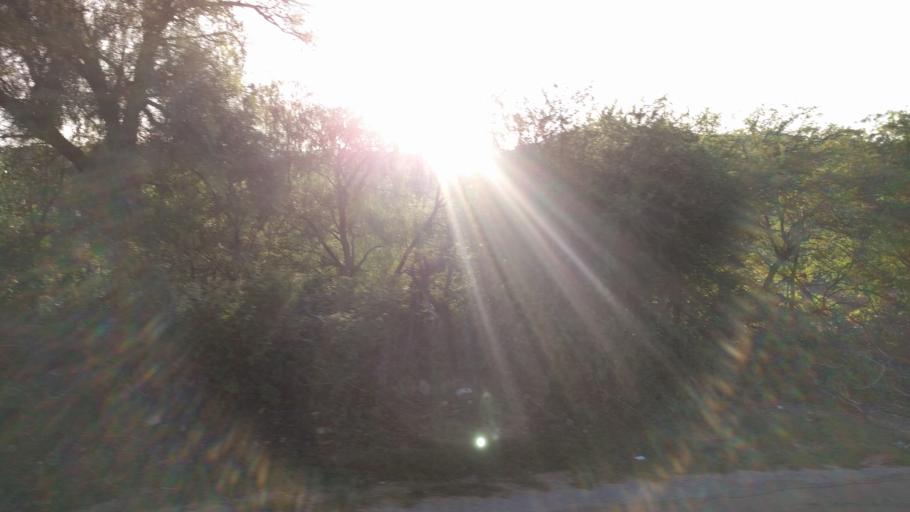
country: BO
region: Tarija
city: Tarija
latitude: -21.5271
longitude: -64.5743
